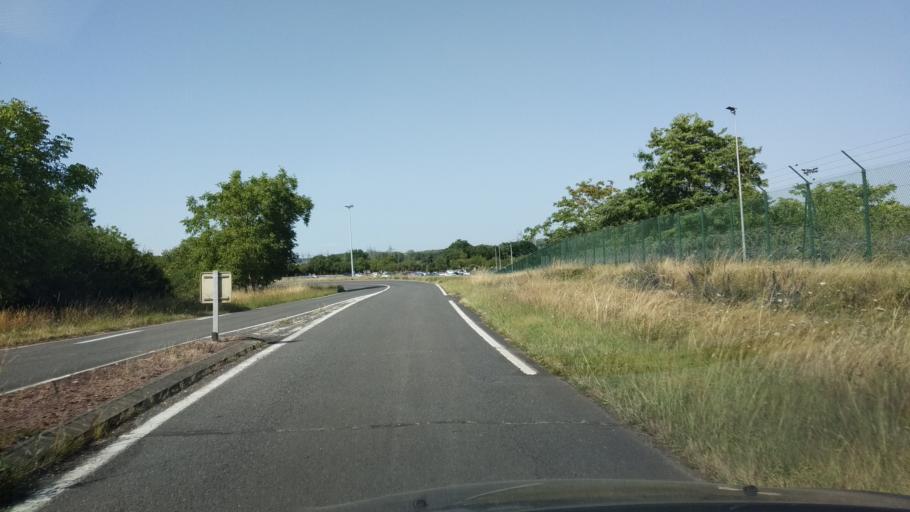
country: FR
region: Poitou-Charentes
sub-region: Departement de la Vienne
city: Lussac-les-Chateaux
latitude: 46.4592
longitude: 0.6462
